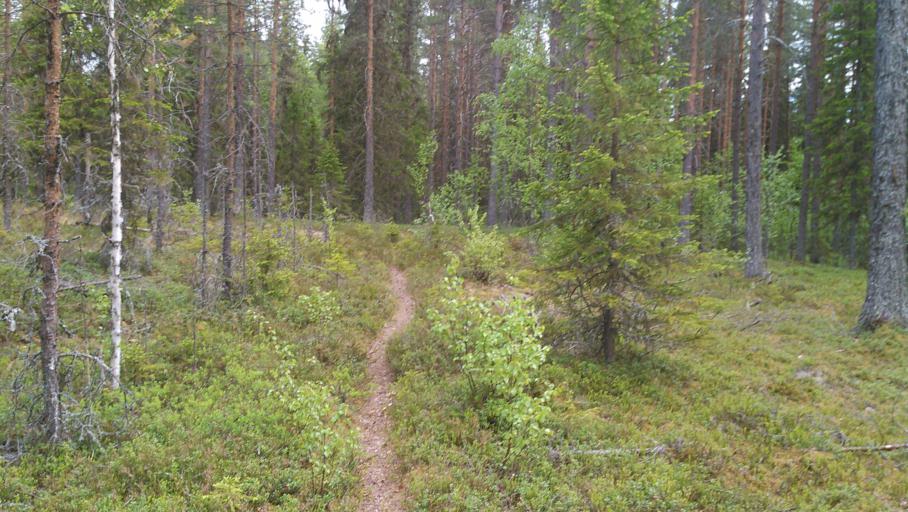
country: SE
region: Vaesterbotten
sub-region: Vannas Kommun
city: Vannasby
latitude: 64.0136
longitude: 19.9157
